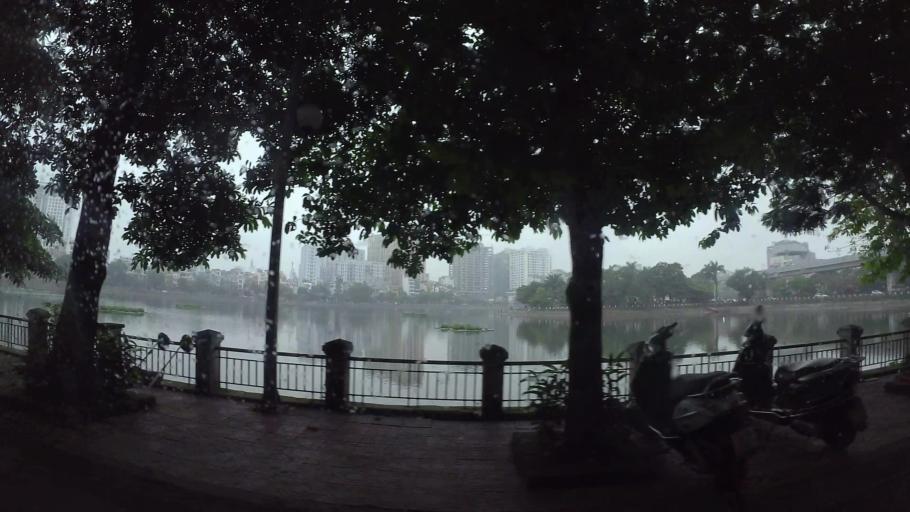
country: VN
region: Ha Noi
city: Dong Da
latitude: 21.0164
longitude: 105.8194
